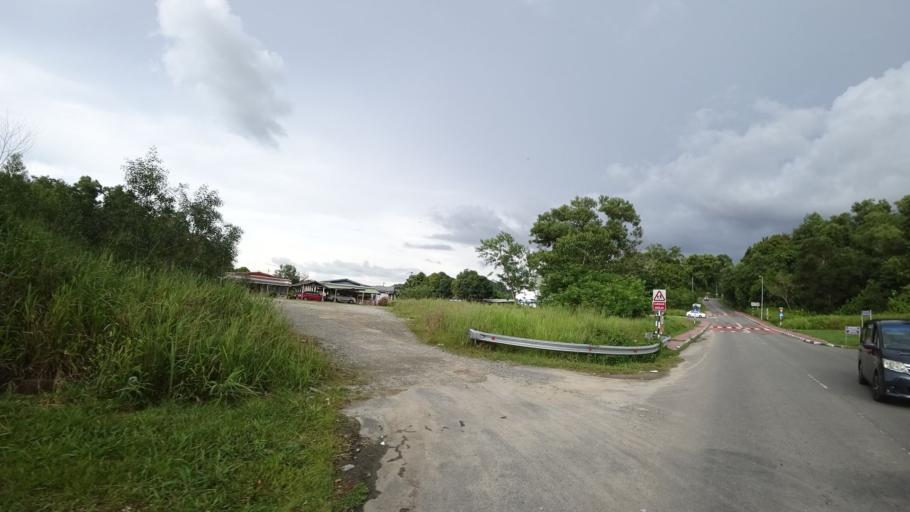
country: BN
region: Brunei and Muara
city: Bandar Seri Begawan
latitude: 4.8648
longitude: 114.9450
